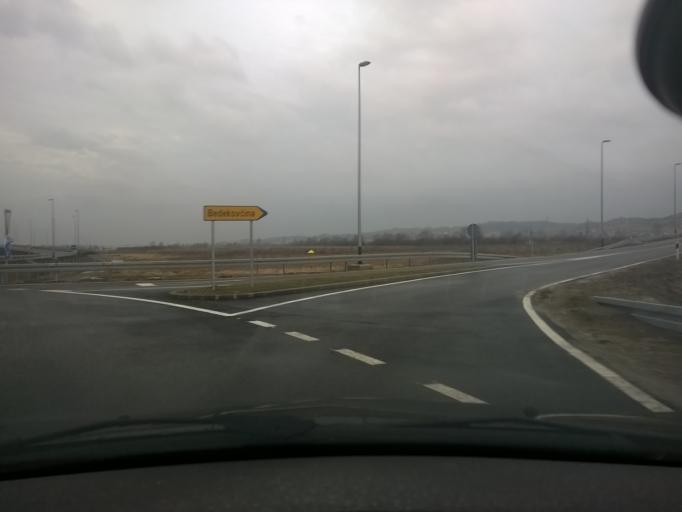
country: HR
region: Krapinsko-Zagorska
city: Bedekovcina
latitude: 46.0337
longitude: 15.9939
